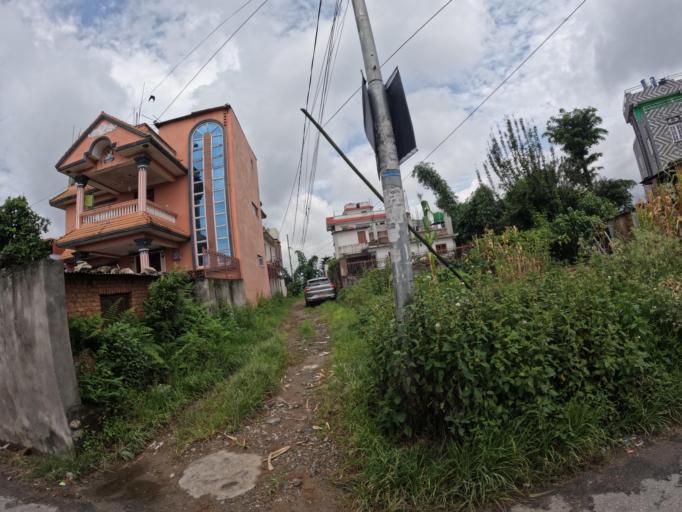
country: NP
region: Central Region
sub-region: Bagmati Zone
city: Kathmandu
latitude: 27.7542
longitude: 85.3215
